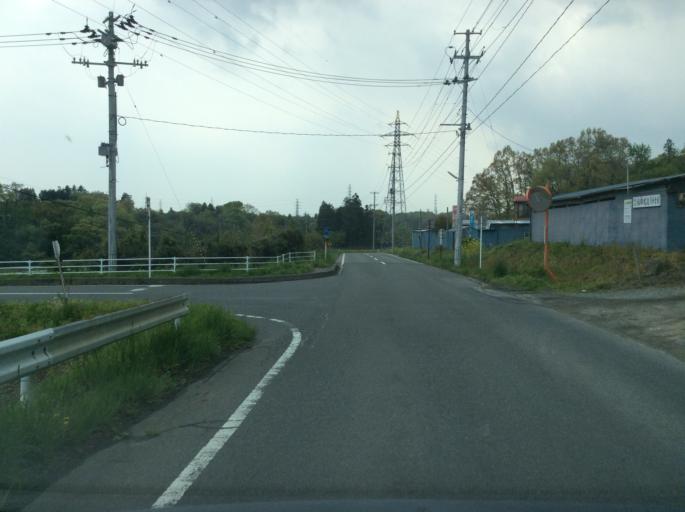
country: JP
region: Fukushima
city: Koriyama
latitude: 37.3865
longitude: 140.4263
